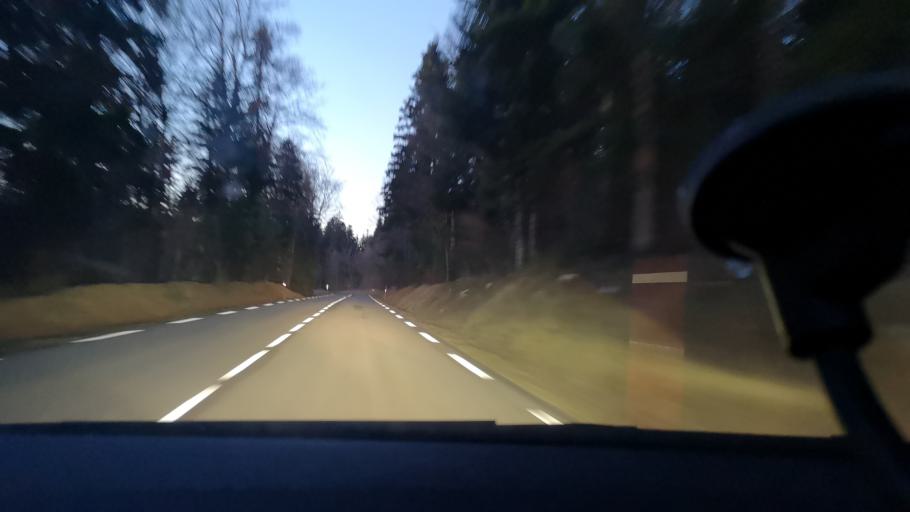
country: FR
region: Franche-Comte
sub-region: Departement du Jura
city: Champagnole
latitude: 46.7558
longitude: 5.9530
